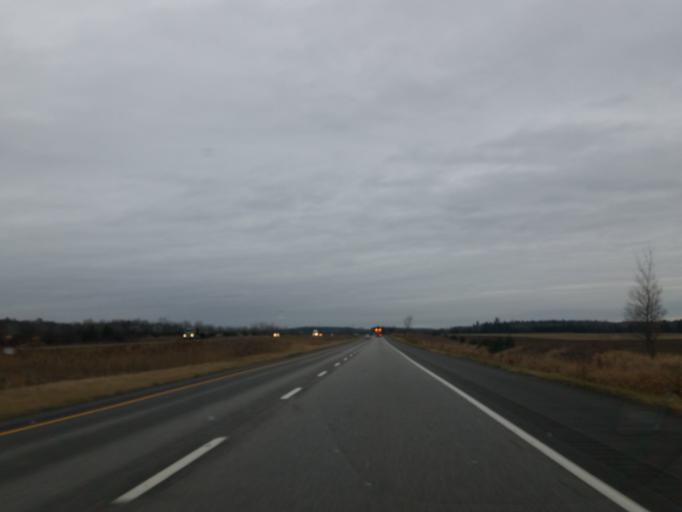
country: CA
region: Quebec
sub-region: Capitale-Nationale
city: Saint-Marc-des-Carrieres
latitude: 46.6737
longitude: -71.9328
